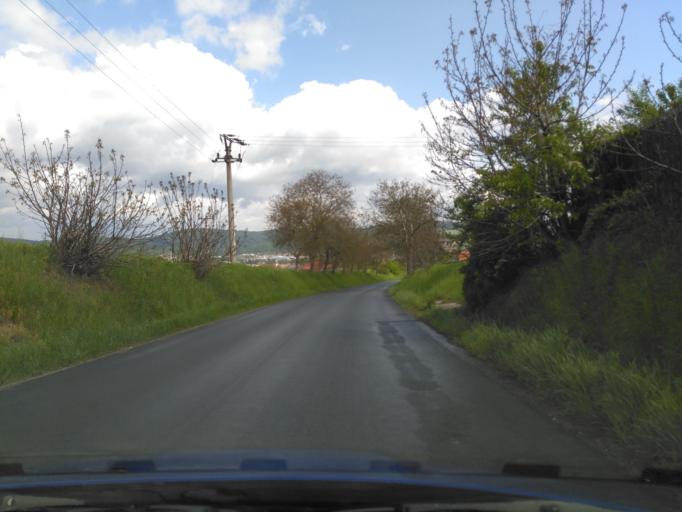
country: CZ
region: Central Bohemia
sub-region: Okres Beroun
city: Beroun
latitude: 49.9447
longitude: 14.0693
